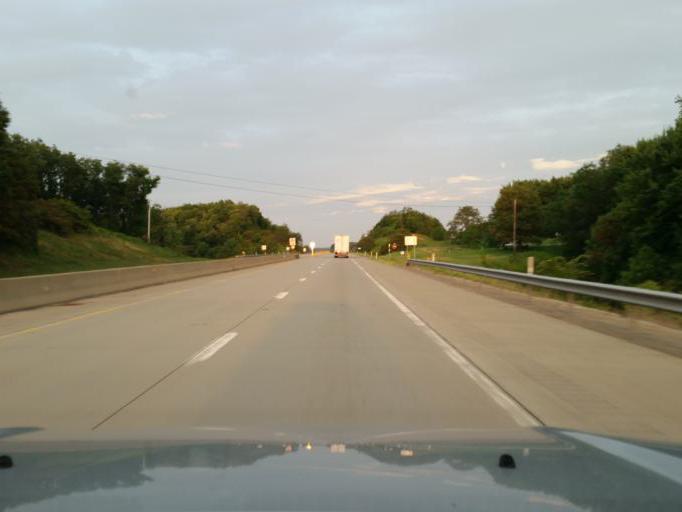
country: US
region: Pennsylvania
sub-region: Cambria County
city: Westmont
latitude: 40.4493
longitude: -78.9877
